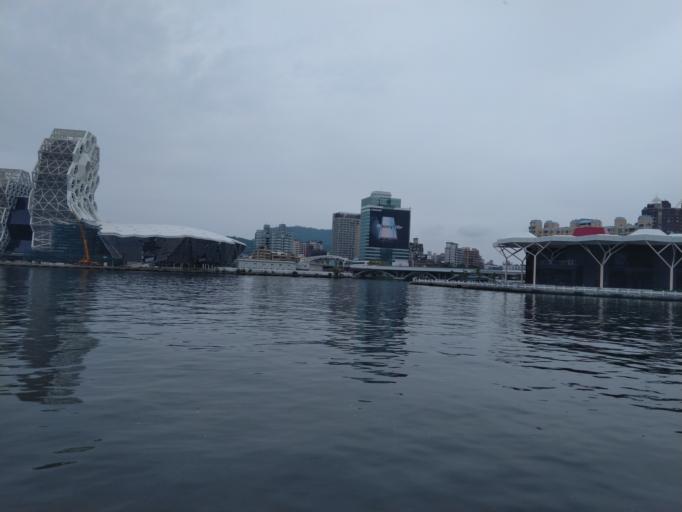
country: TW
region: Kaohsiung
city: Kaohsiung
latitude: 22.6166
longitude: 120.2924
